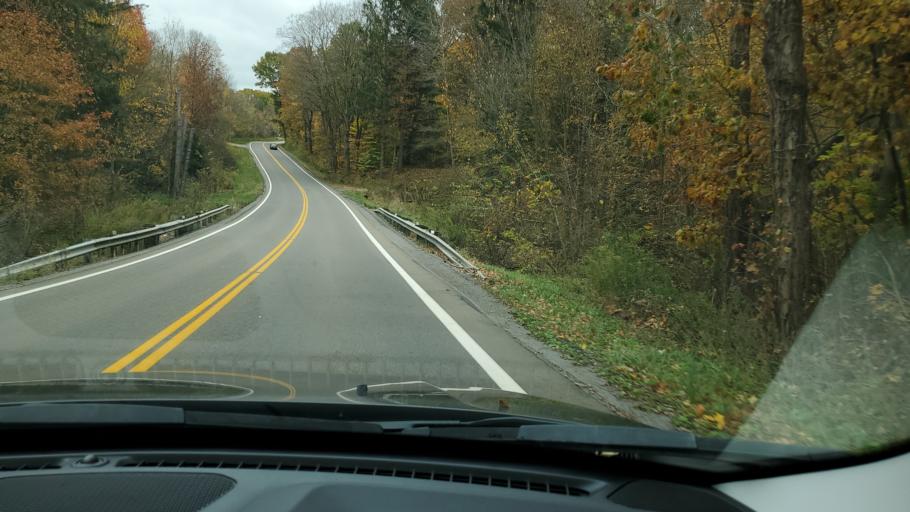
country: US
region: Ohio
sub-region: Columbiana County
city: New Waterford
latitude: 40.8908
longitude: -80.5770
